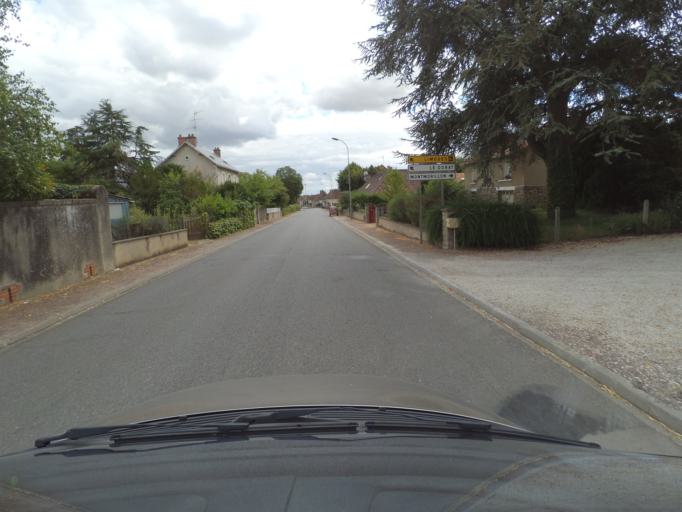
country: FR
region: Centre
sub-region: Departement de l'Indre
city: Belabre
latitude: 46.4695
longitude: 1.0378
